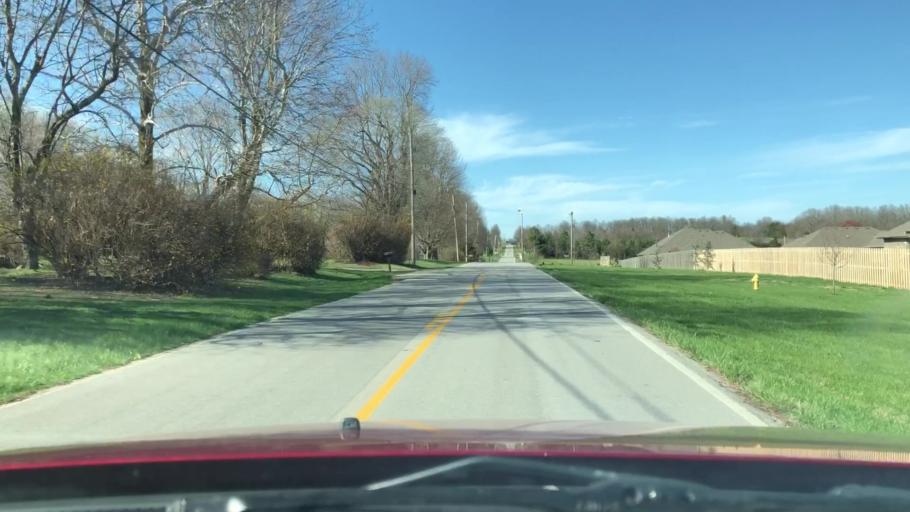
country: US
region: Missouri
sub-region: Greene County
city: Strafford
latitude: 37.2305
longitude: -93.1884
